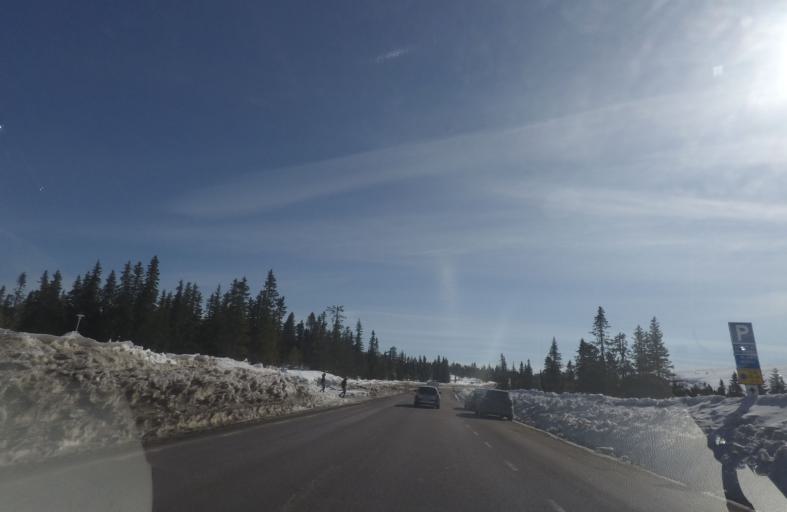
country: SE
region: Dalarna
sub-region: Malung-Saelens kommun
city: Malung
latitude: 61.1631
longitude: 13.1061
